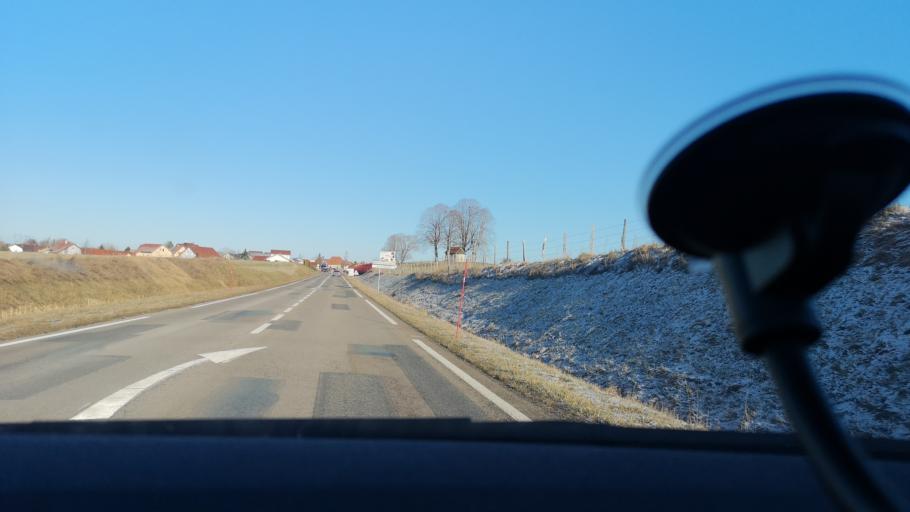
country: FR
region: Franche-Comte
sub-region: Departement du Doubs
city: Frasne
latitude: 46.8484
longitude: 6.1455
